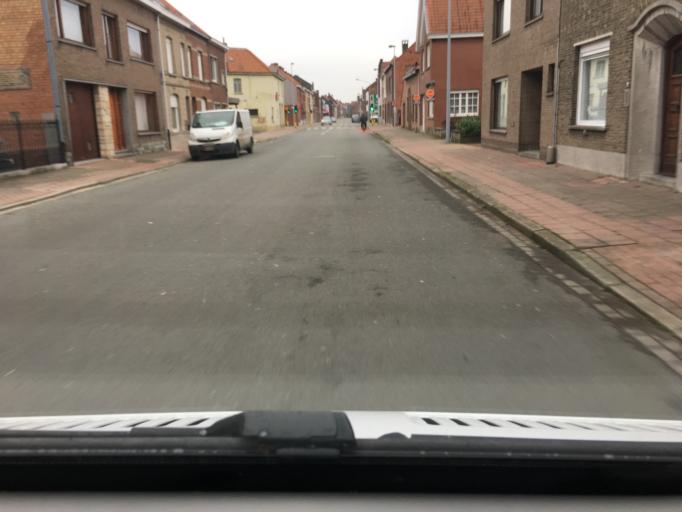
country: BE
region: Flanders
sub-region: Provincie West-Vlaanderen
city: Wervik
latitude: 50.7799
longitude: 3.0330
